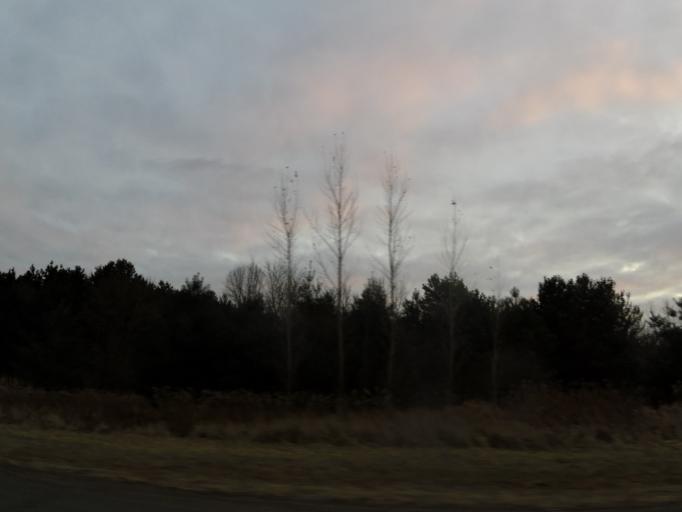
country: US
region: Minnesota
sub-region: Washington County
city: Mahtomedi
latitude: 45.0571
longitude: -92.9435
